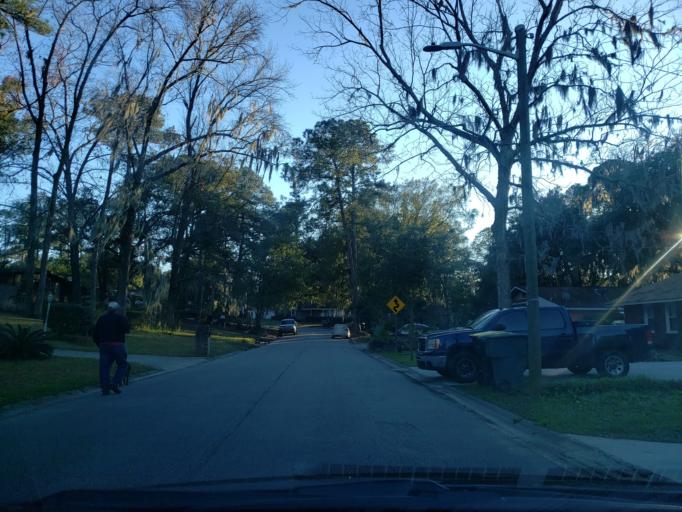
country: US
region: Georgia
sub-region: Chatham County
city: Isle of Hope
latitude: 31.9936
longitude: -81.1112
